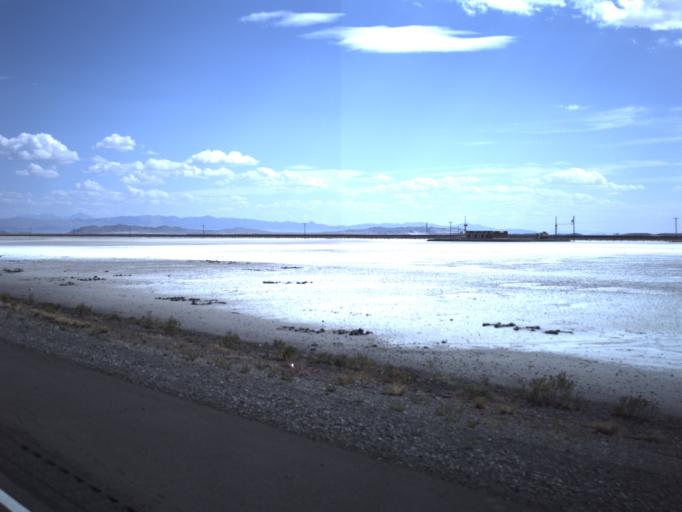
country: US
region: Utah
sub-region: Tooele County
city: Wendover
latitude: 40.7295
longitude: -113.4412
